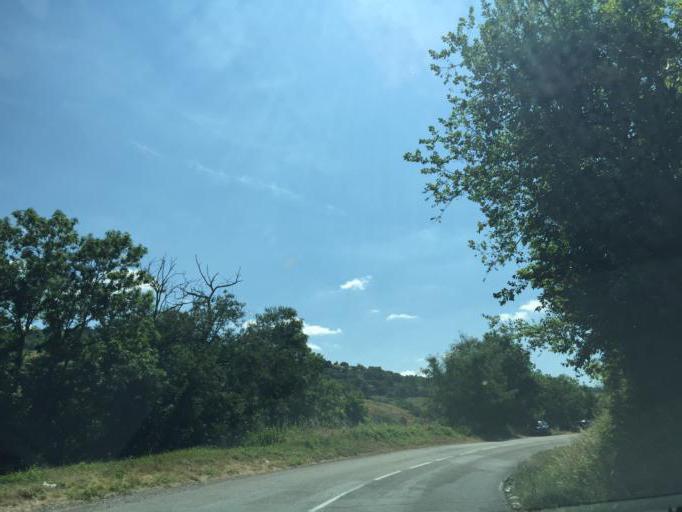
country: FR
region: Rhone-Alpes
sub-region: Departement de la Loire
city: Saint-Chamond
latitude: 45.4391
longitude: 4.5101
